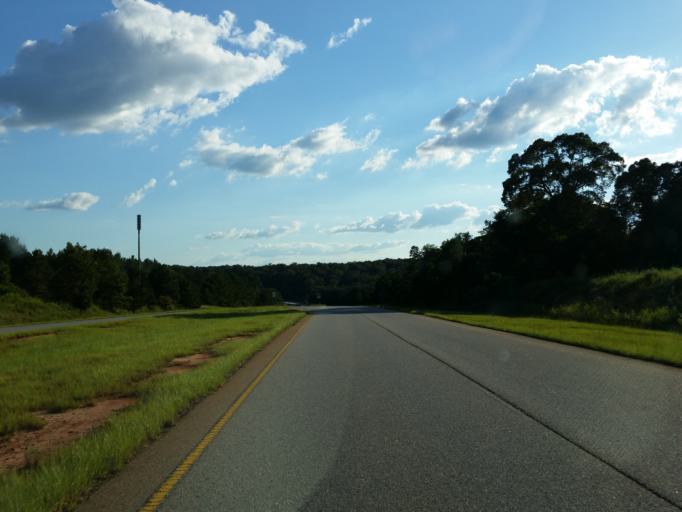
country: US
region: Georgia
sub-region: Houston County
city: Perry
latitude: 32.4801
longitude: -83.7731
